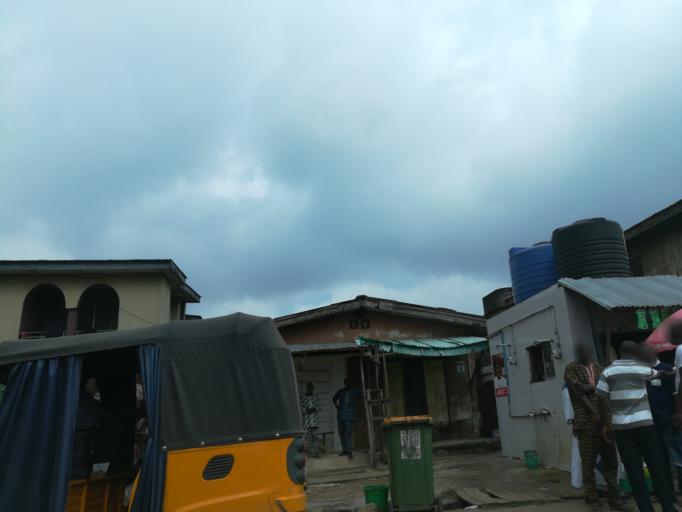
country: NG
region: Lagos
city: Oshodi
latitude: 6.5808
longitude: 3.3029
